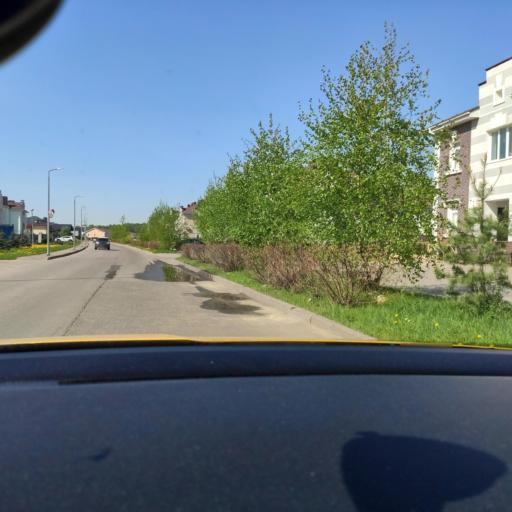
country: RU
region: Moskovskaya
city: Nakhabino
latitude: 55.8877
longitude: 37.1796
